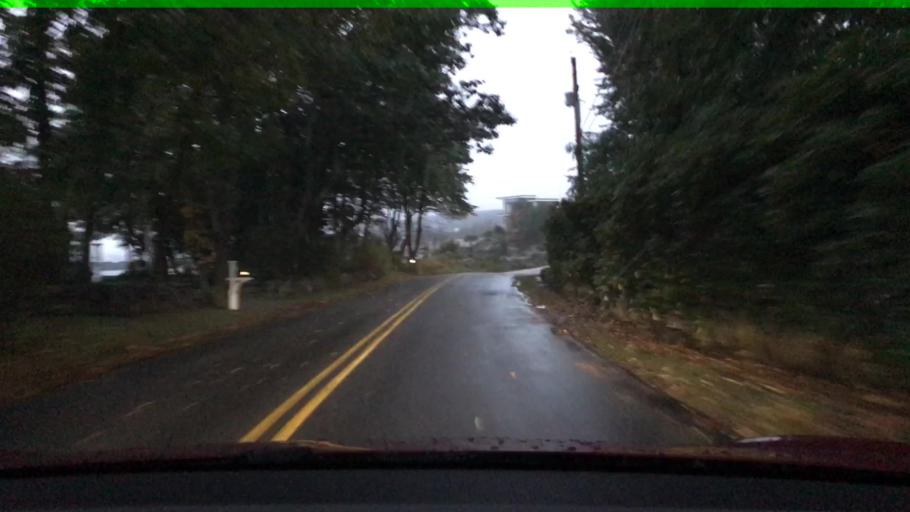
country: US
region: Maine
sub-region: York County
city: Cape Neddick
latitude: 43.2099
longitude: -70.5880
